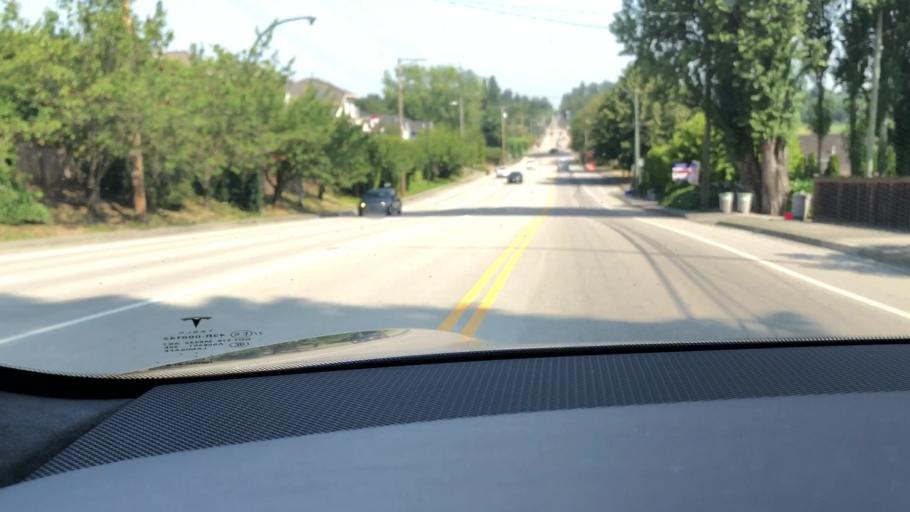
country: US
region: Washington
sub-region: Whatcom County
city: Point Roberts
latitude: 49.0075
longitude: -123.0687
